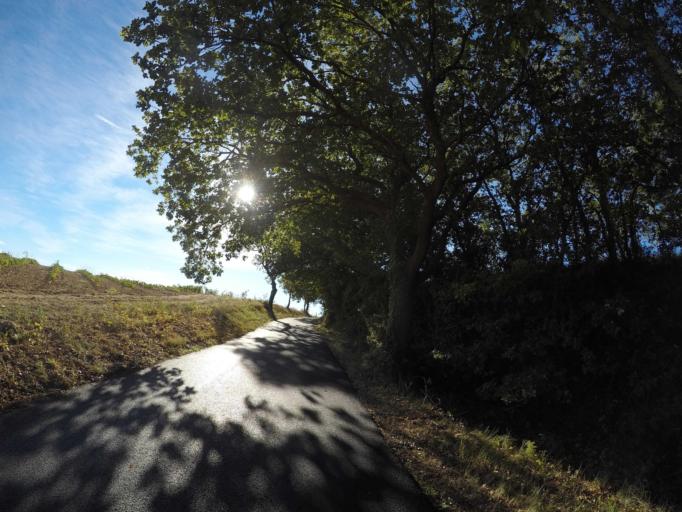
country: FR
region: Languedoc-Roussillon
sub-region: Departement des Pyrenees-Orientales
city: Trouillas
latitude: 42.5778
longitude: 2.7847
